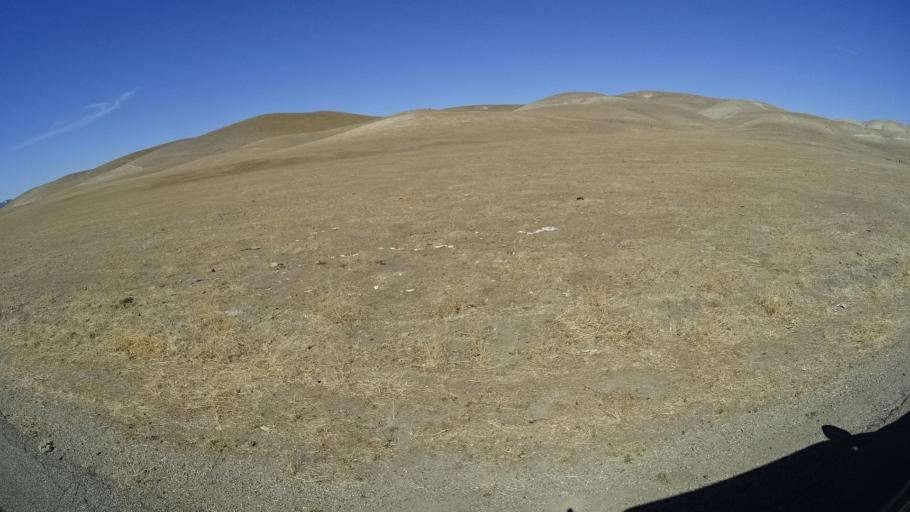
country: US
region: California
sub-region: San Luis Obispo County
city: Lake Nacimiento
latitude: 36.0422
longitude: -120.8331
